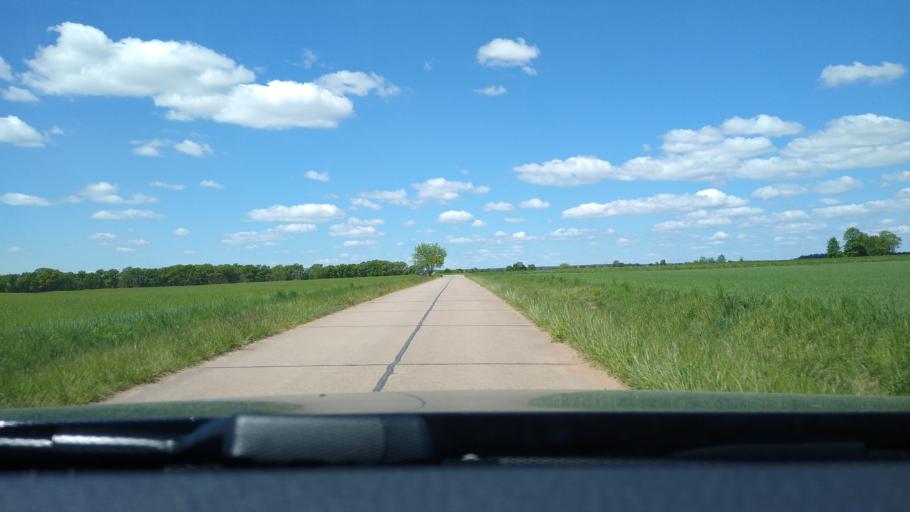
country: DE
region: Bavaria
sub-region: Regierungsbezirk Mittelfranken
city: Obermichelbach
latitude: 49.5120
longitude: 10.9499
